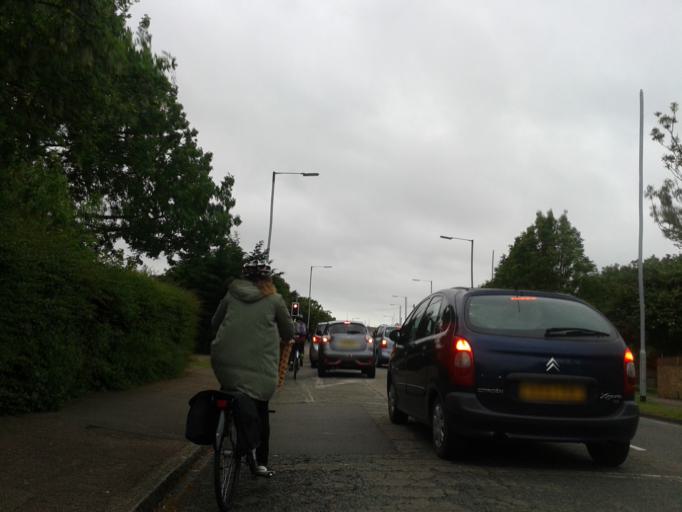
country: GB
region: England
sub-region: Cambridgeshire
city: Cambridge
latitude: 52.2226
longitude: 0.1123
